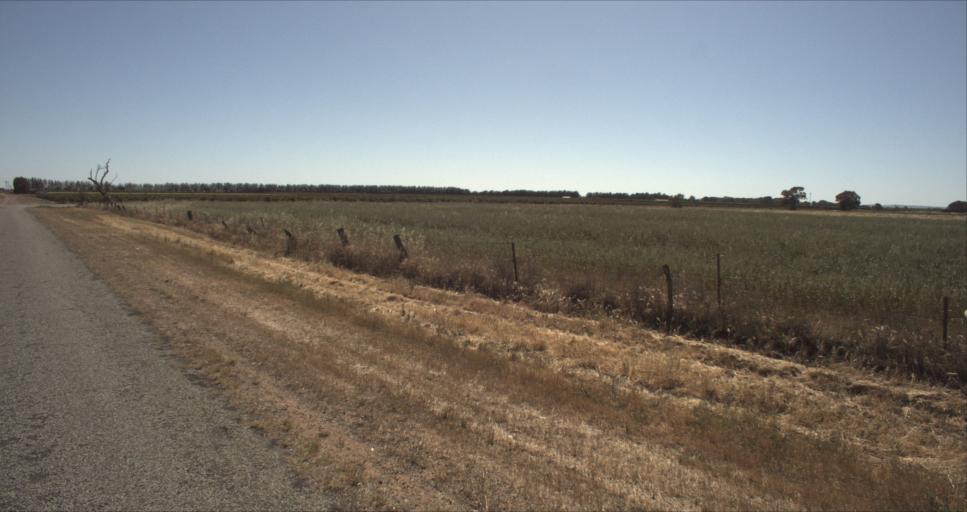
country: AU
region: New South Wales
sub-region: Leeton
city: Leeton
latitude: -34.5340
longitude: 146.3178
